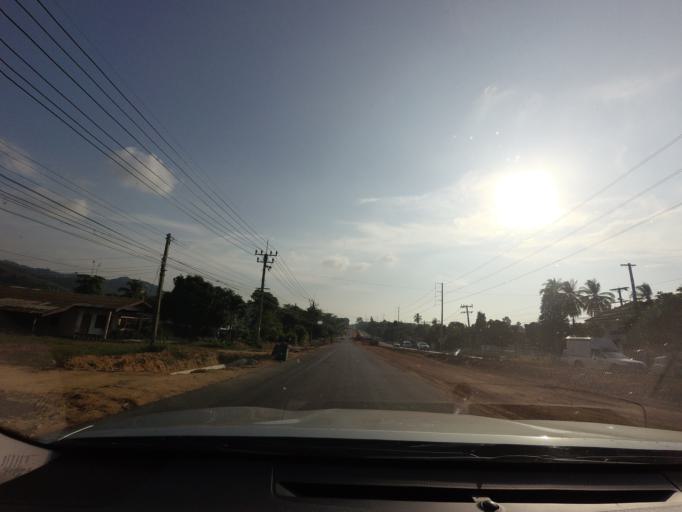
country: TH
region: Phangnga
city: Ban Khao Lak
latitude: 8.7499
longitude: 98.2632
